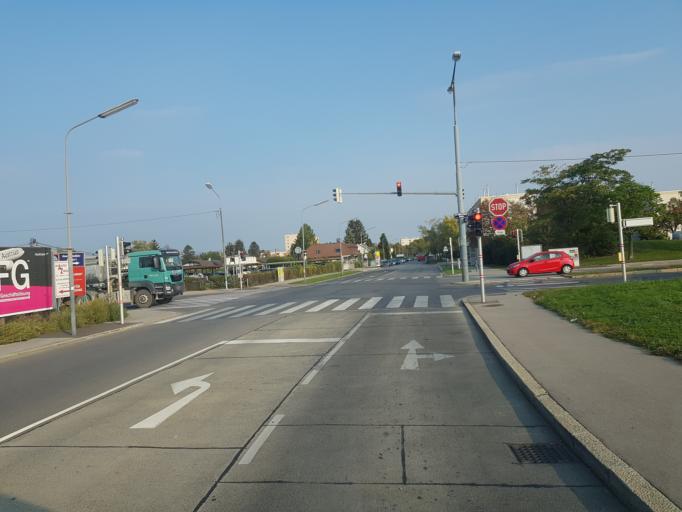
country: AT
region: Lower Austria
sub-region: Politischer Bezirk Wien-Umgebung
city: Gerasdorf bei Wien
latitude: 48.2656
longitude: 16.4398
